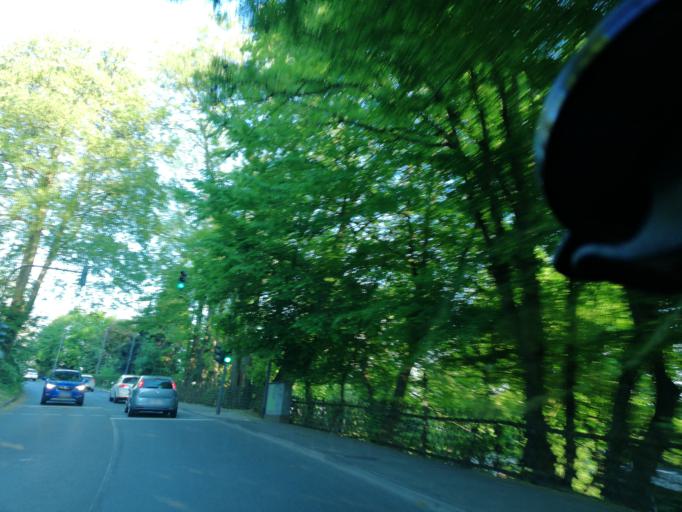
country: DE
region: North Rhine-Westphalia
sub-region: Regierungsbezirk Dusseldorf
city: Wuppertal
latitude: 51.2626
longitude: 7.2004
